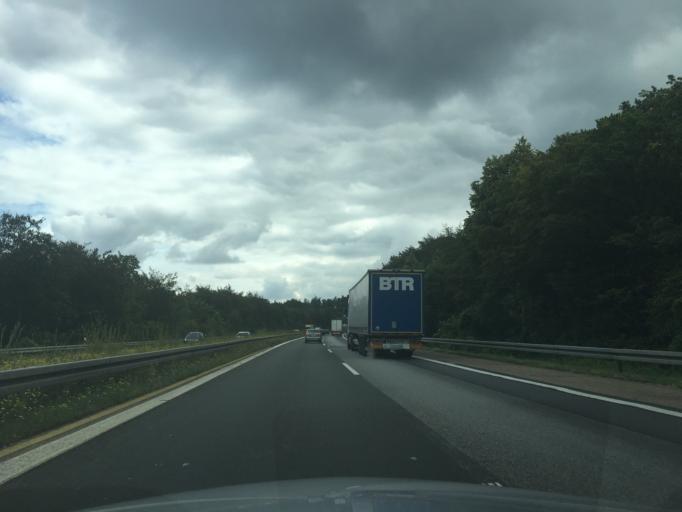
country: DE
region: Bavaria
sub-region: Regierungsbezirk Unterfranken
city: Geiselwind
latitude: 49.7836
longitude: 10.4147
